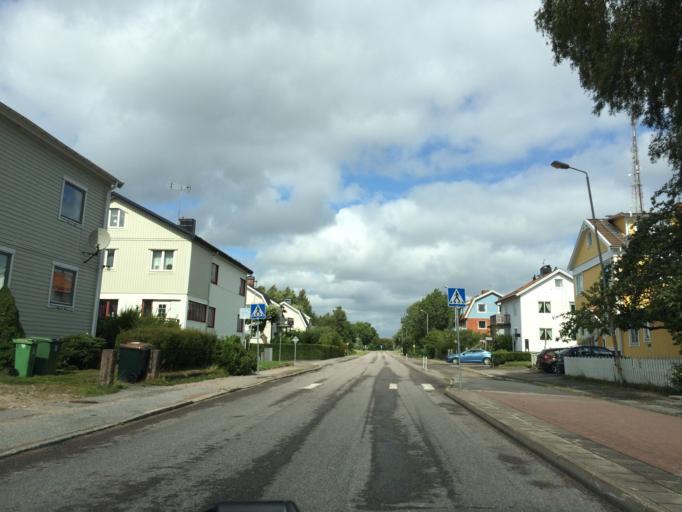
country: SE
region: Vaestra Goetaland
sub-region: Trollhattan
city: Trollhattan
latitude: 58.2878
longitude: 12.2727
